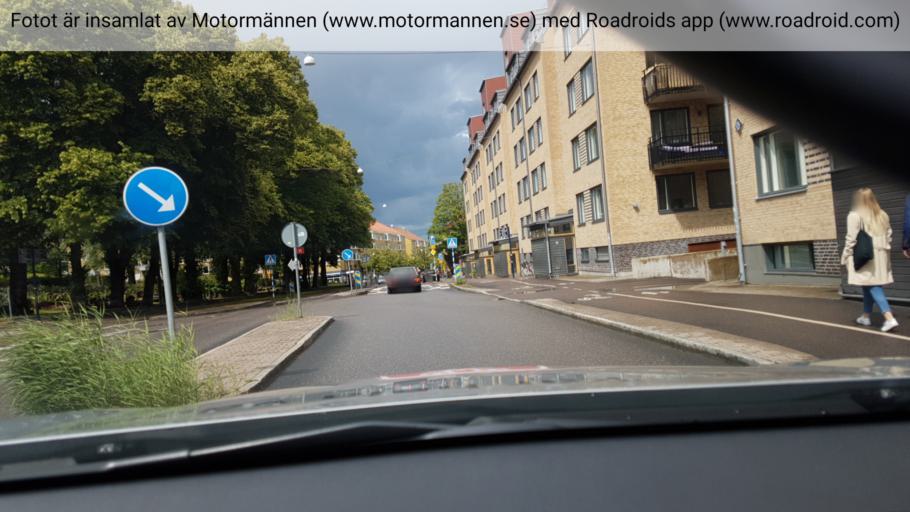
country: SE
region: Vaestra Goetaland
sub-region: Goteborg
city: Goeteborg
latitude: 57.7096
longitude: 12.0074
